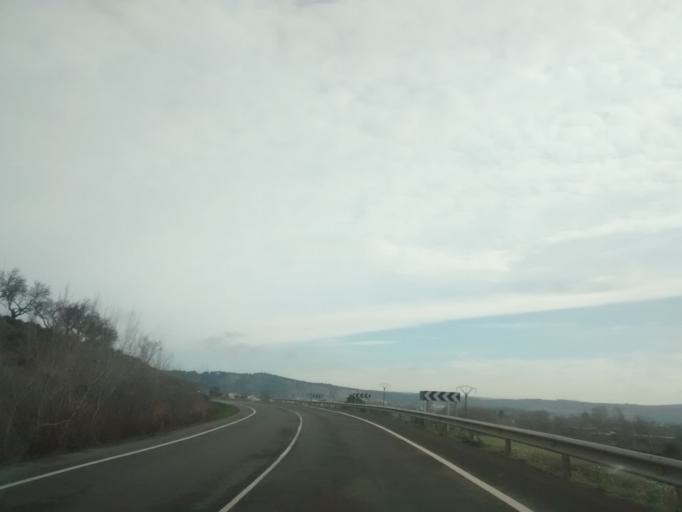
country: ES
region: La Rioja
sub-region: Provincia de La Rioja
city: Alcanadre
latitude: 42.4204
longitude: -2.1045
